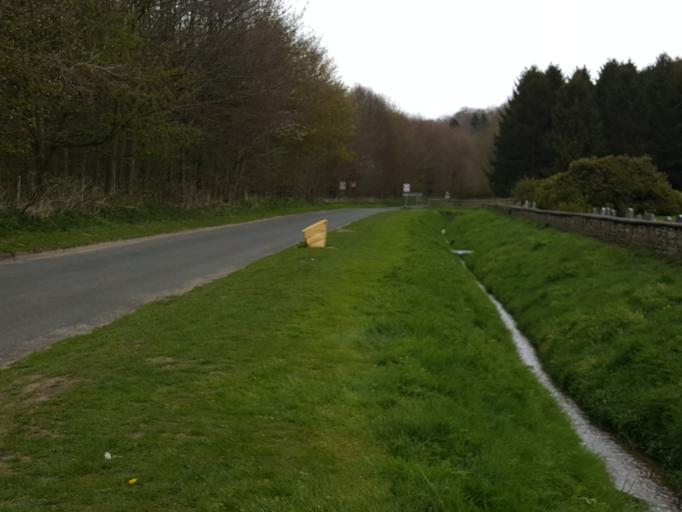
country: GB
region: England
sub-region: East Riding of Yorkshire
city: Brantingham
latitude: 53.7582
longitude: -0.5706
